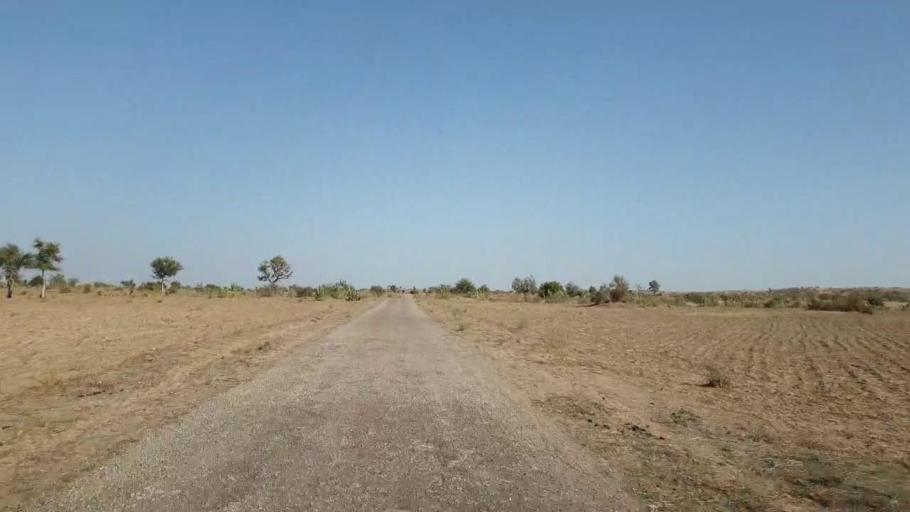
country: PK
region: Sindh
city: Islamkot
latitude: 25.0317
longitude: 70.0383
